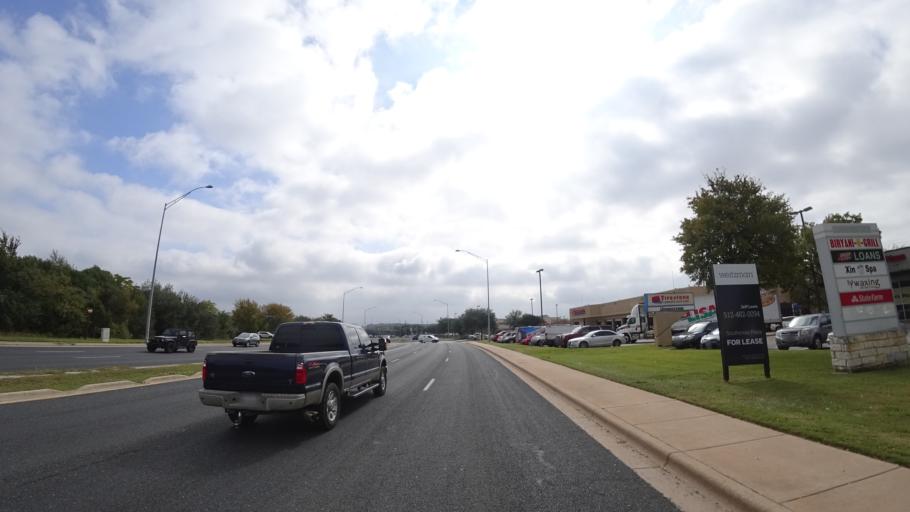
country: US
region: Texas
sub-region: Travis County
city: Shady Hollow
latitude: 30.2151
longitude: -97.8328
